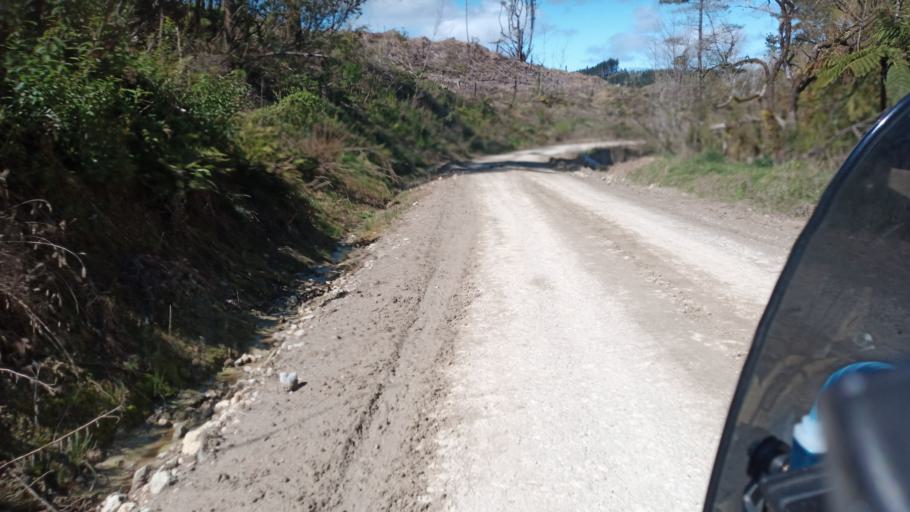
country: NZ
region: Gisborne
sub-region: Gisborne District
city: Gisborne
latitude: -38.8896
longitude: 177.7907
